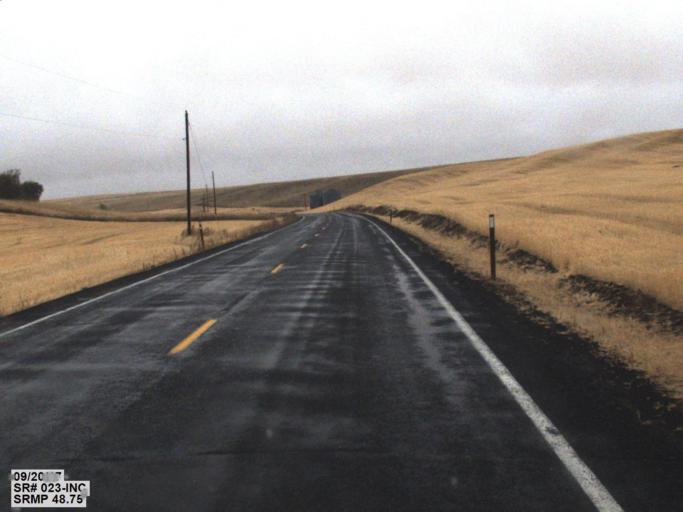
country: US
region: Washington
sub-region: Lincoln County
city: Davenport
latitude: 47.3551
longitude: -118.0345
